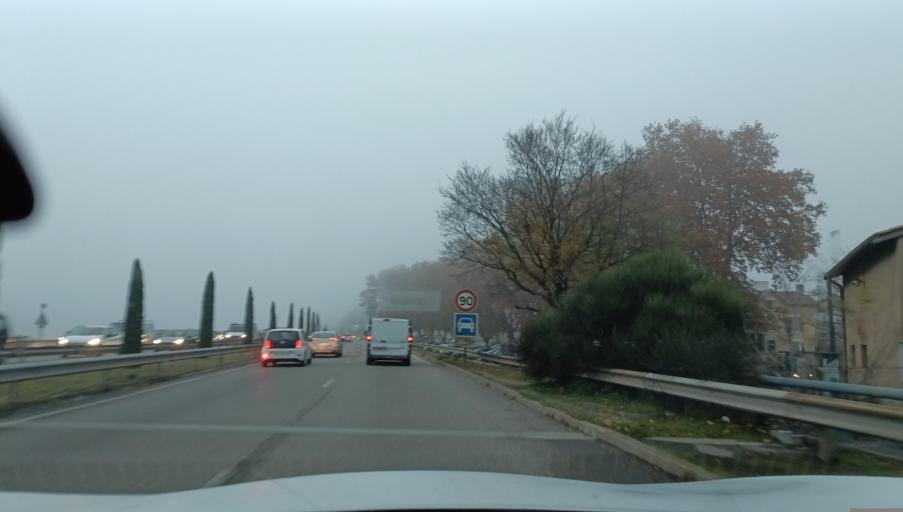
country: FR
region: Rhone-Alpes
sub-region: Departement du Rhone
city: Saint-Romain-en-Gal
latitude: 45.5365
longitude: 4.8697
